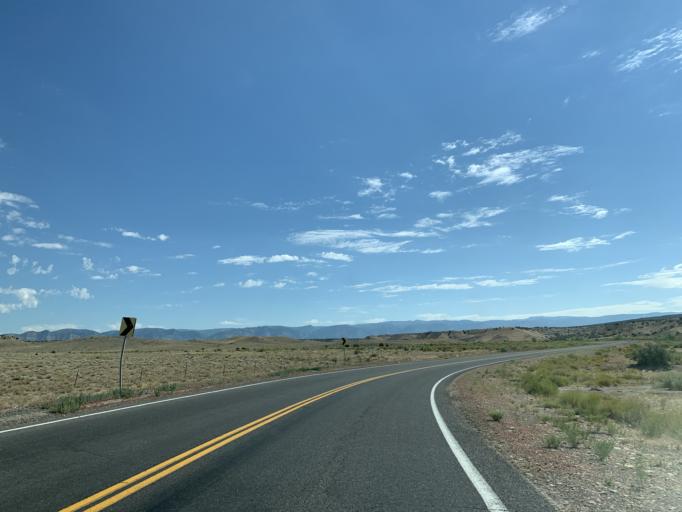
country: US
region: Utah
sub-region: Carbon County
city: Wellington
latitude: 39.5591
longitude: -110.6646
